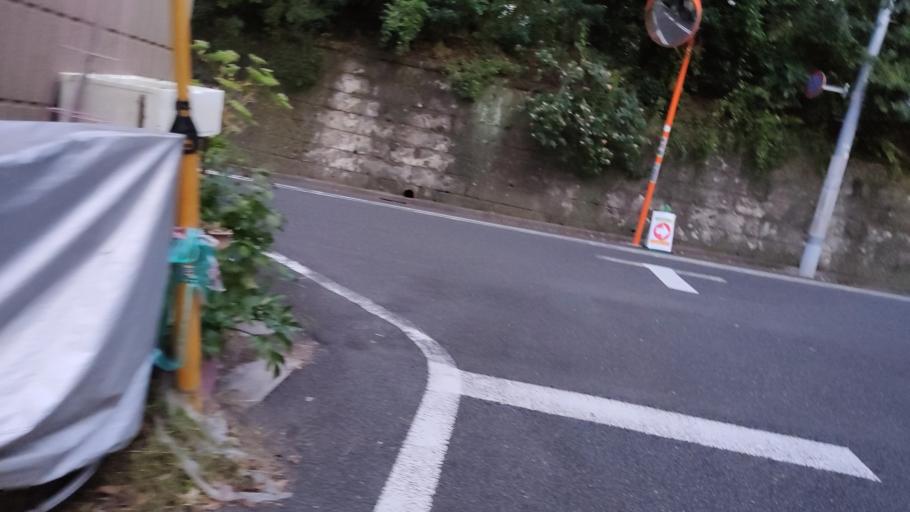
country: JP
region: Tokyo
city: Tokyo
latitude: 35.6364
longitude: 139.6765
